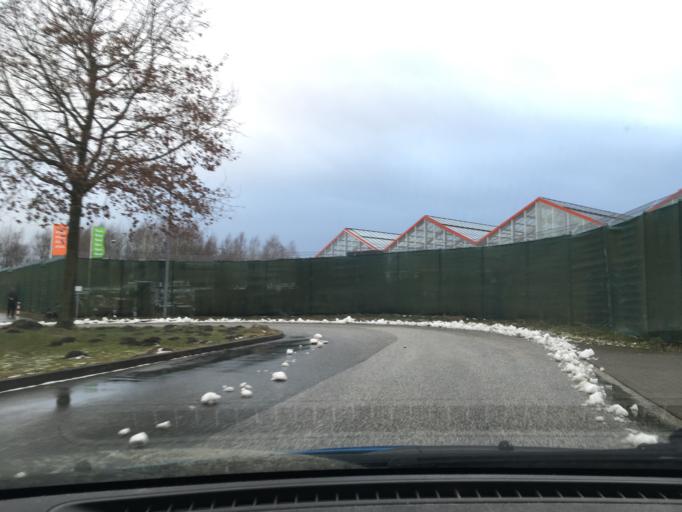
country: DE
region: Schleswig-Holstein
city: Ottenbuttel
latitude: 53.9579
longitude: 9.4945
